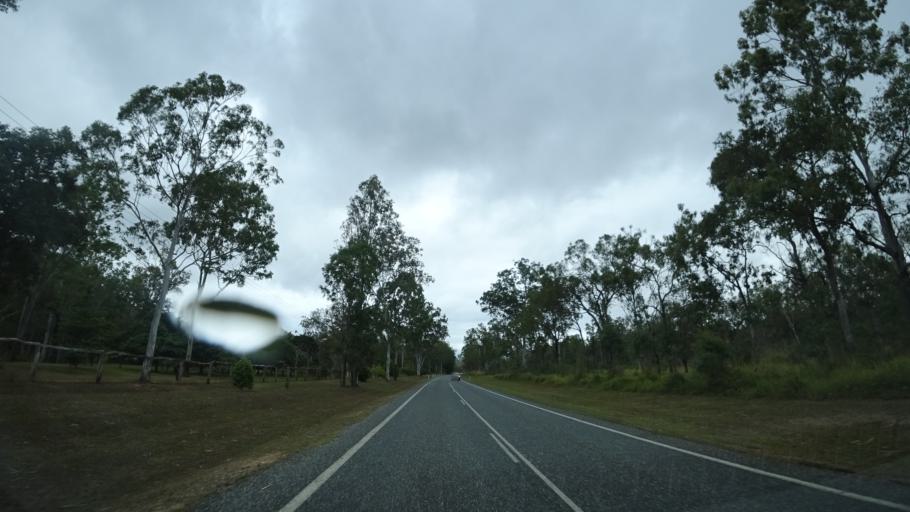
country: AU
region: Queensland
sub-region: Cairns
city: Port Douglas
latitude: -16.7303
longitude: 145.3522
